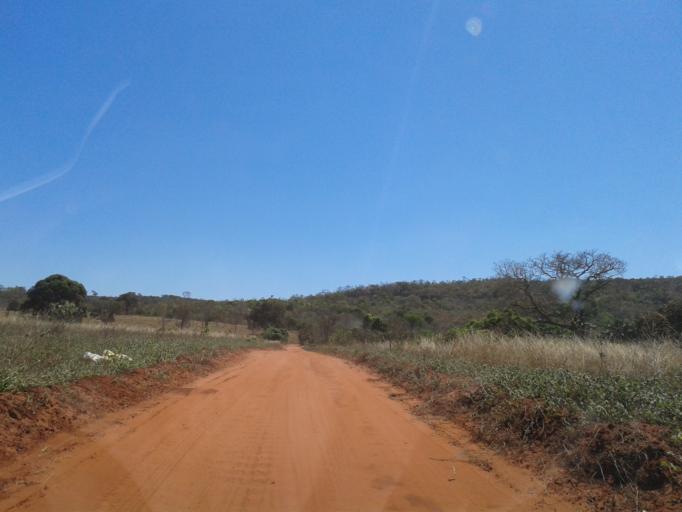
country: BR
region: Minas Gerais
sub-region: Ituiutaba
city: Ituiutaba
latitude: -19.1001
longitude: -49.2957
